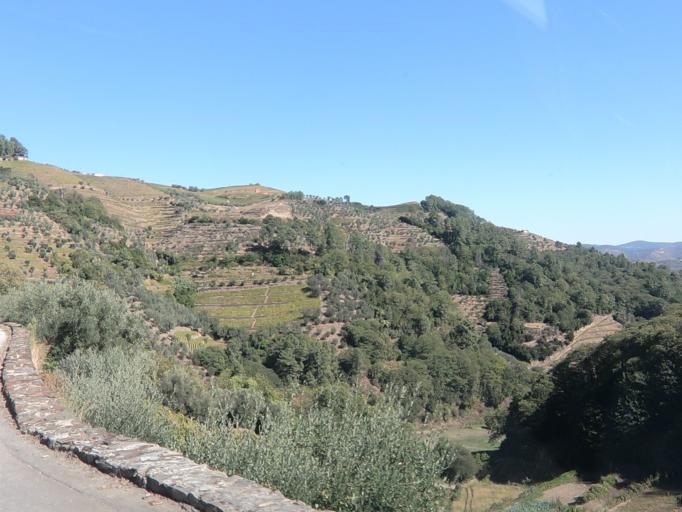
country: PT
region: Vila Real
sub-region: Santa Marta de Penaguiao
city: Santa Marta de Penaguiao
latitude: 41.2417
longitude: -7.8072
